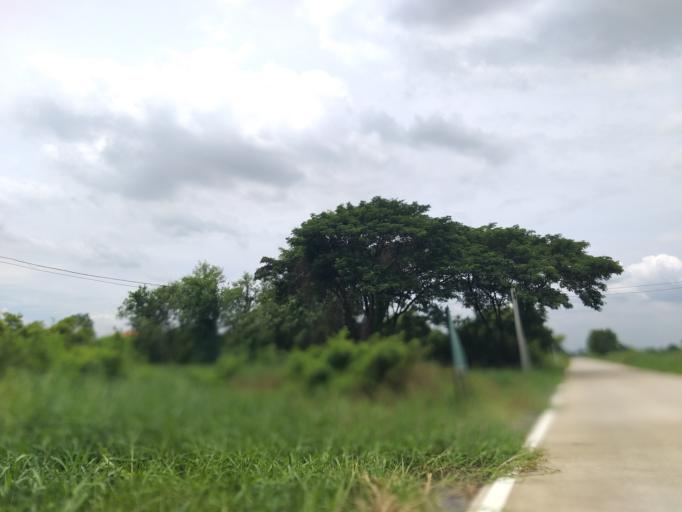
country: TH
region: Pathum Thani
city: Ban Lam Luk Ka
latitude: 13.9745
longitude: 100.8530
